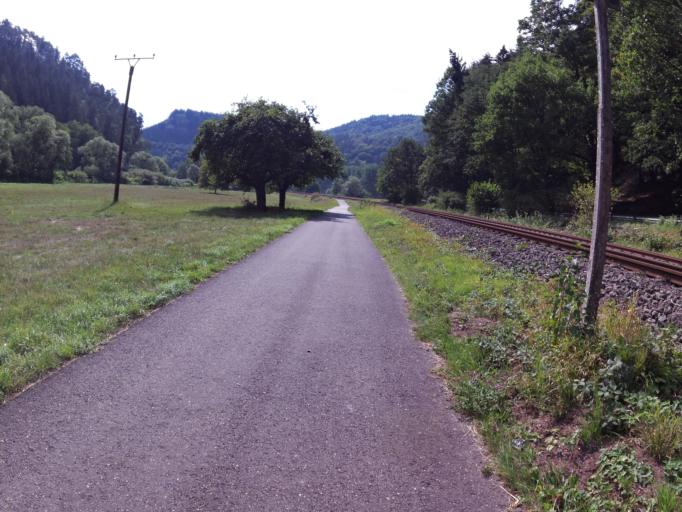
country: DE
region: Rheinland-Pfalz
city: Kordel
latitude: 49.8275
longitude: 6.6500
